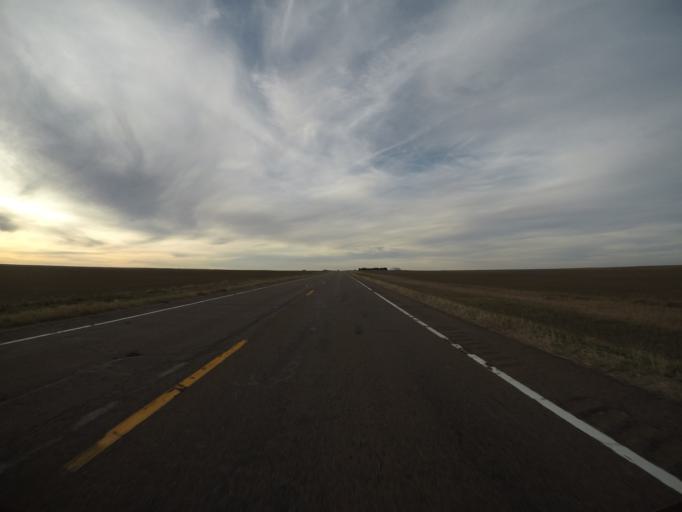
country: US
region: Colorado
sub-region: Yuma County
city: Yuma
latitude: 39.6801
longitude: -102.9655
